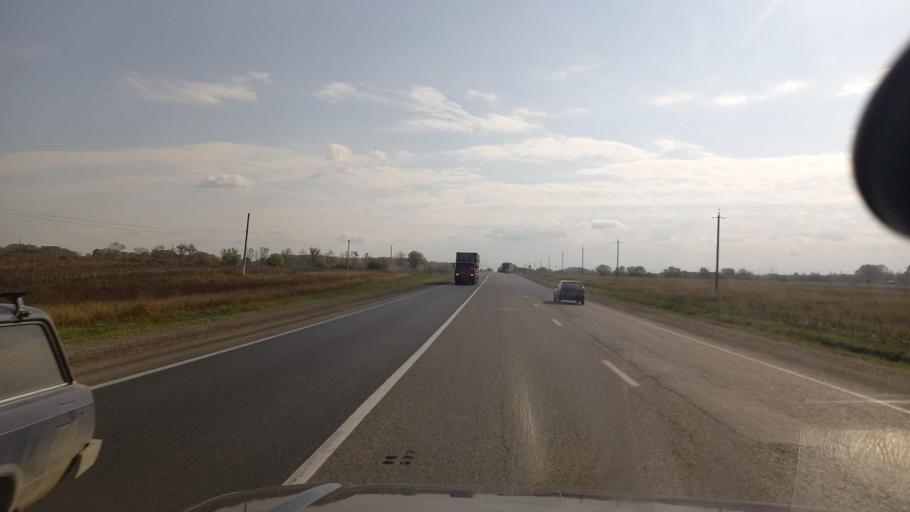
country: RU
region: Krasnodarskiy
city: Novoukrainskiy
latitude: 44.8921
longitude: 38.0680
